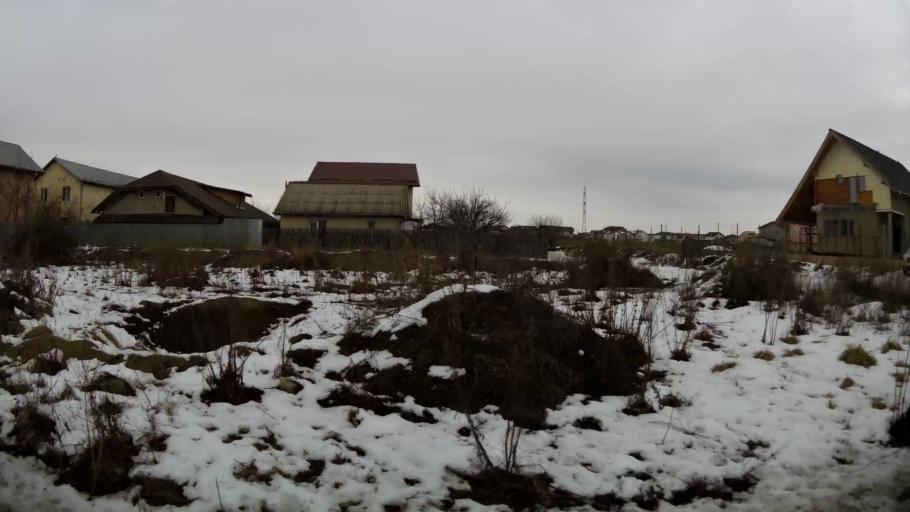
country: RO
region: Ilfov
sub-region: Comuna Pantelimon
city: Pantelimon
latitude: 44.4567
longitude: 26.2175
